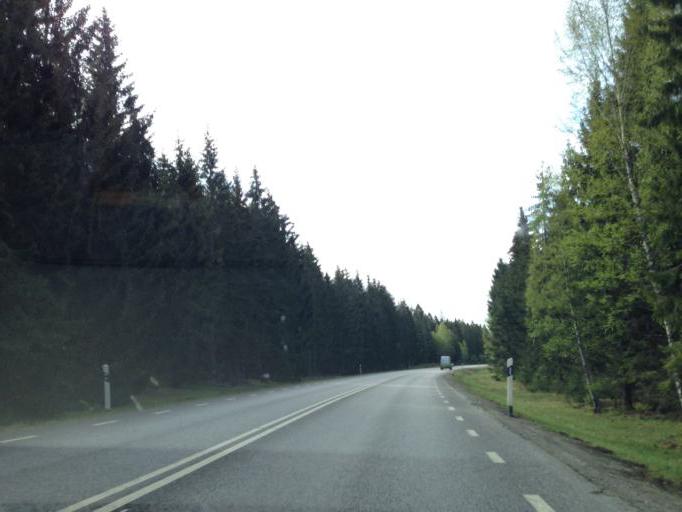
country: SE
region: Soedermanland
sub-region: Nykopings Kommun
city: Svalsta
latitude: 58.8506
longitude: 16.9209
